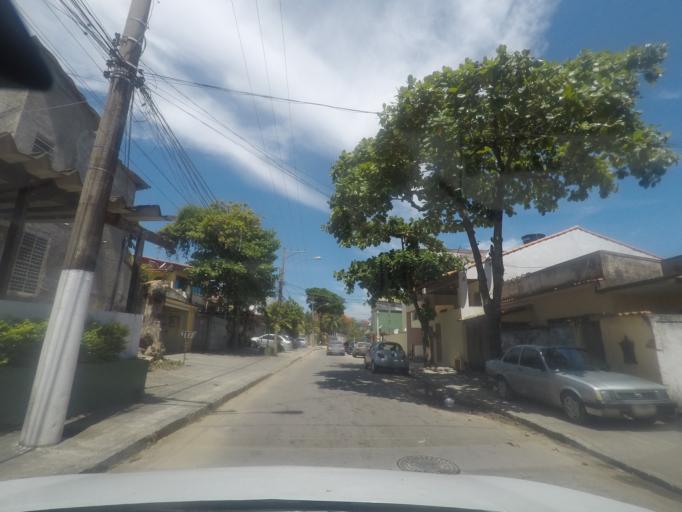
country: BR
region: Rio de Janeiro
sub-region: Itaguai
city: Itaguai
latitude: -23.0052
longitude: -43.6361
